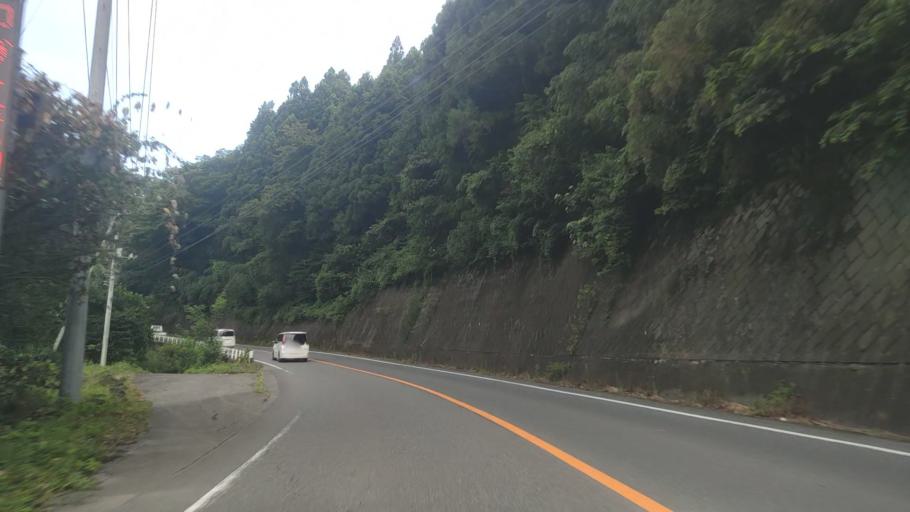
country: JP
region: Gunma
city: Omamacho-omama
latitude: 36.4940
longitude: 139.2750
